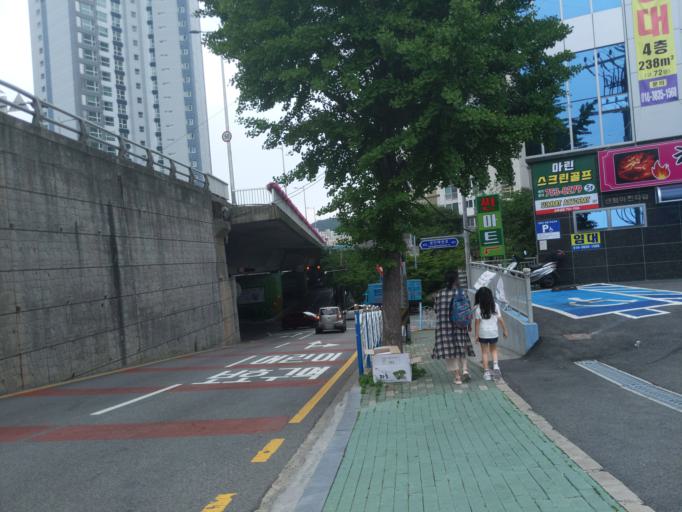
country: KR
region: Busan
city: Busan
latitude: 35.1602
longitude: 129.1291
